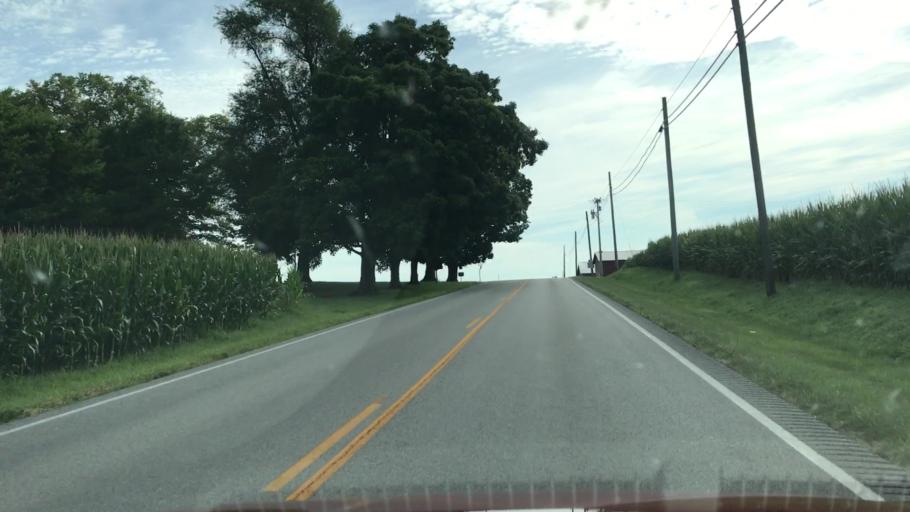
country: US
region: Kentucky
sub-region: Edmonson County
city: Brownsville
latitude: 37.0584
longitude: -86.2966
